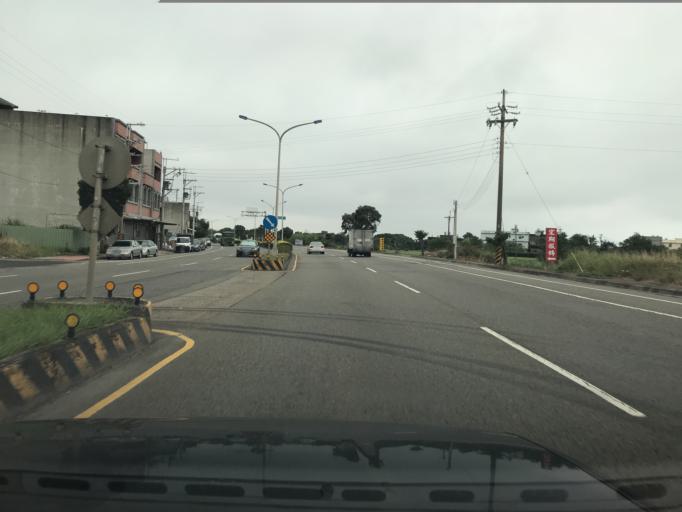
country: TW
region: Taiwan
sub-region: Hsinchu
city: Hsinchu
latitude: 24.8315
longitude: 120.9267
